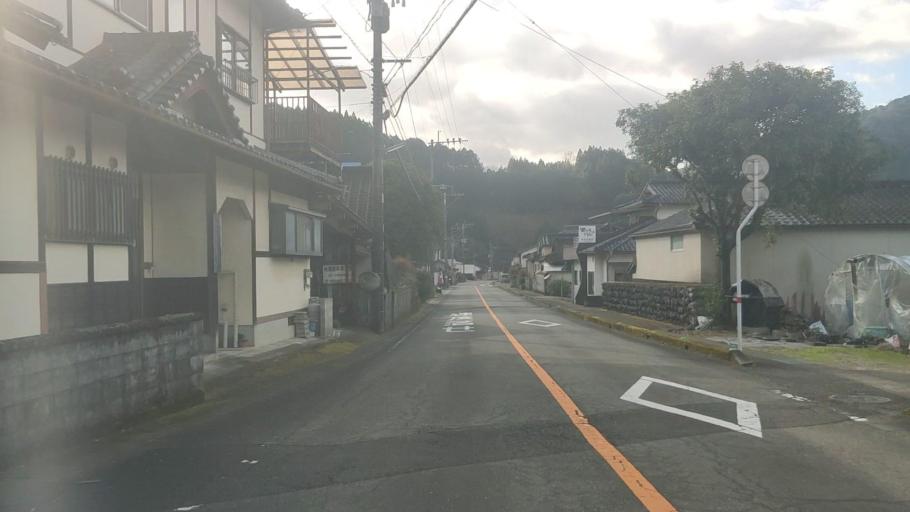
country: JP
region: Kumamoto
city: Hitoyoshi
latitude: 32.3065
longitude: 130.8477
